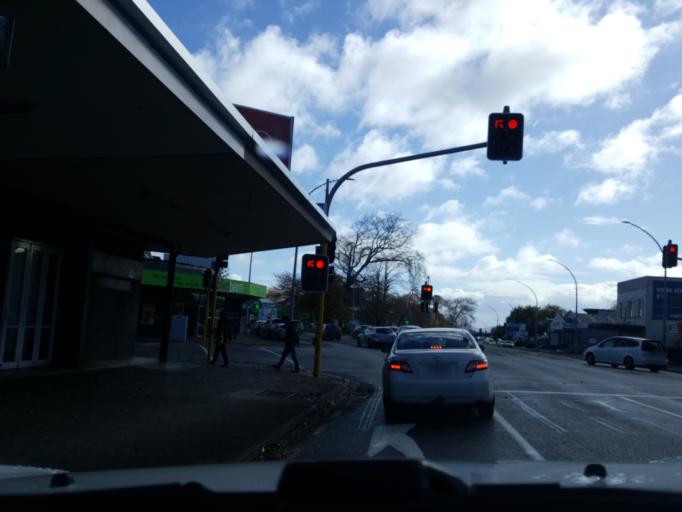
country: NZ
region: Waikato
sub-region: Hamilton City
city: Hamilton
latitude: -37.7800
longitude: 175.2763
